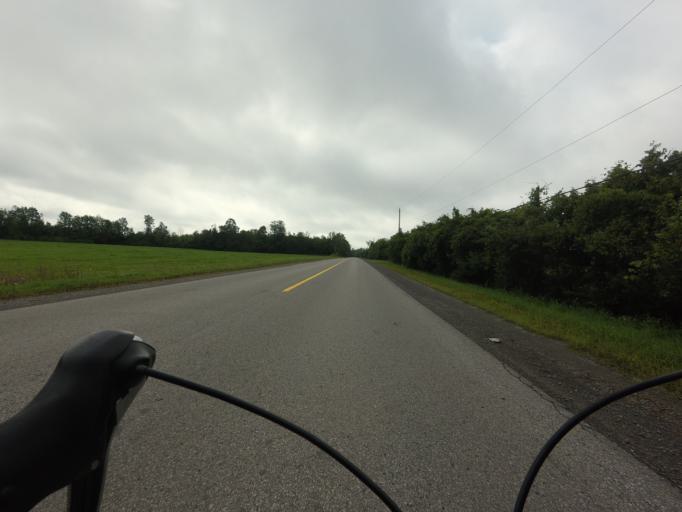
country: CA
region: Ontario
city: Bells Corners
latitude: 45.0718
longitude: -75.7342
